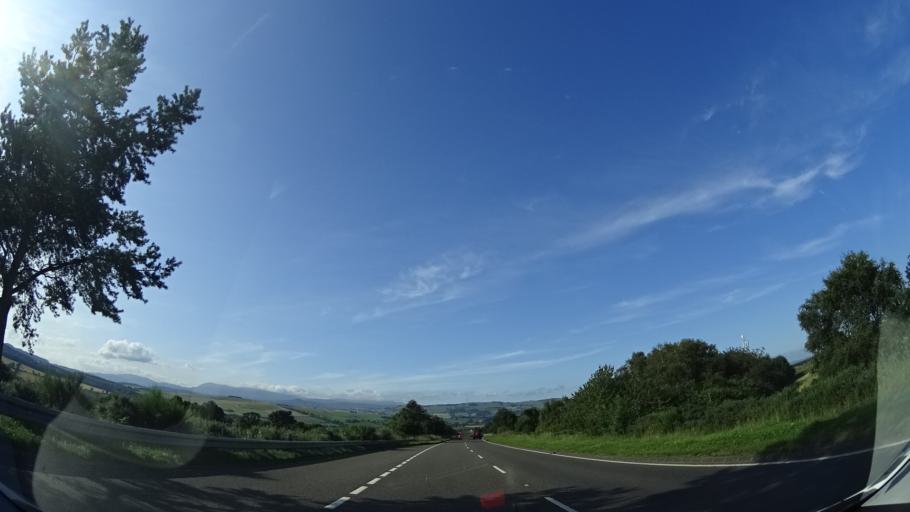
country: GB
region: Scotland
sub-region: Highland
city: Conon Bridge
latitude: 57.5587
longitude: -4.4187
